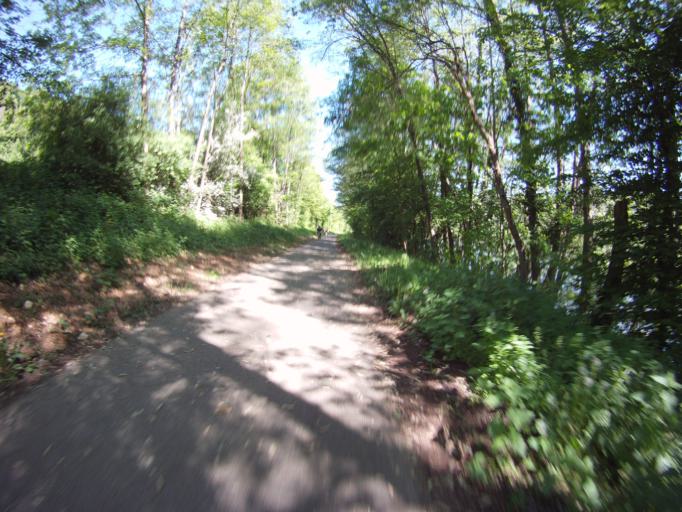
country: FR
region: Lorraine
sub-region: Departement de Meurthe-et-Moselle
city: Chaligny
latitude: 48.6388
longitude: 6.0398
